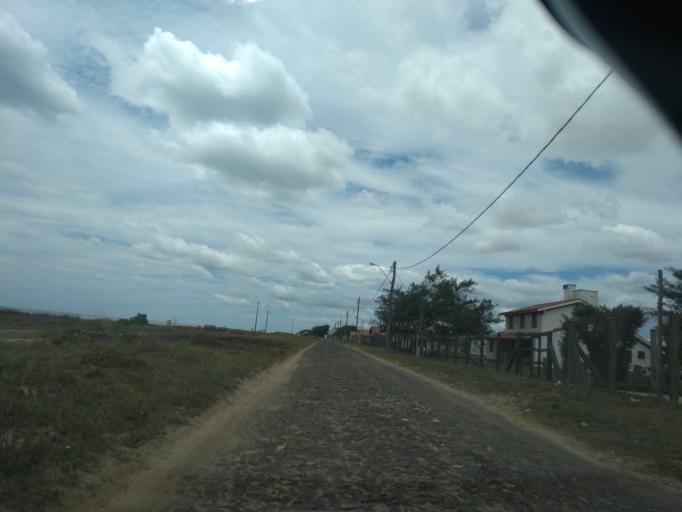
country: BR
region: Rio Grande do Sul
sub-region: Tramandai
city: Tramandai
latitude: -30.0645
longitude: -50.1586
